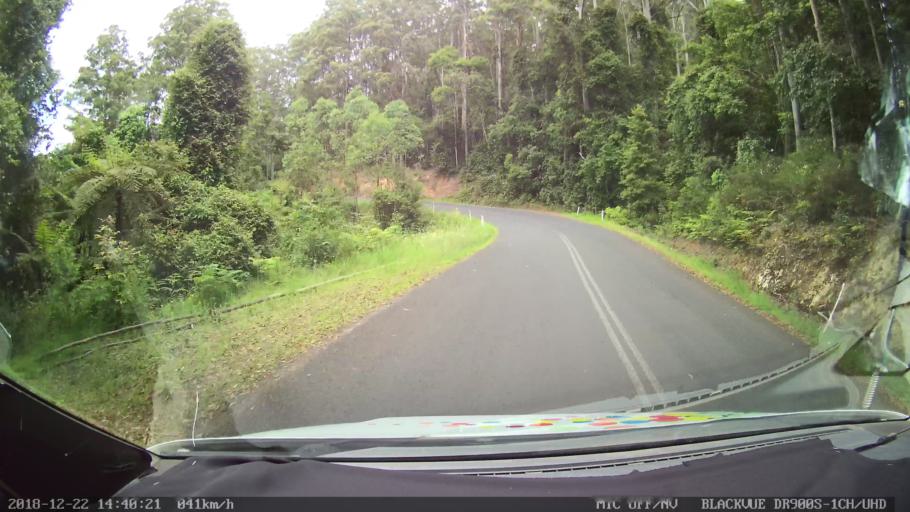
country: AU
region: New South Wales
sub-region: Bellingen
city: Dorrigo
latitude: -30.1502
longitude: 152.5887
